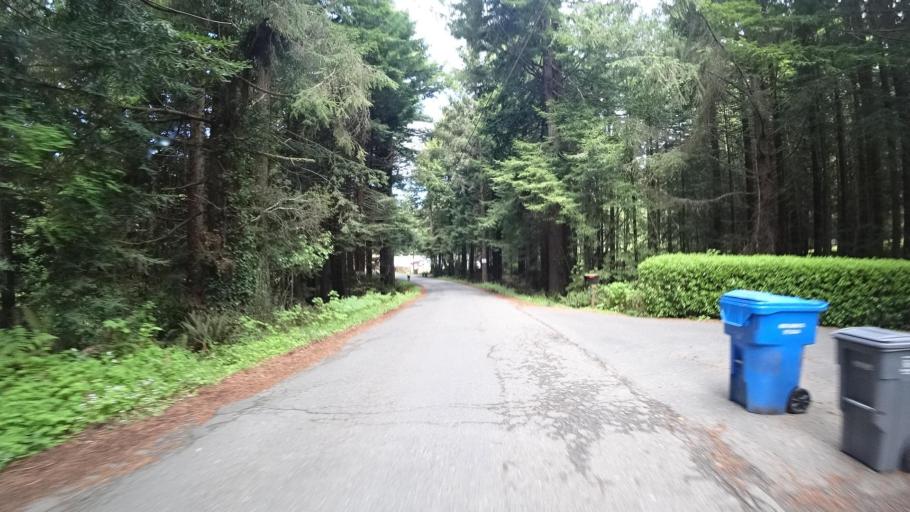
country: US
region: California
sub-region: Humboldt County
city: Bayside
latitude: 40.8494
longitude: -124.0557
